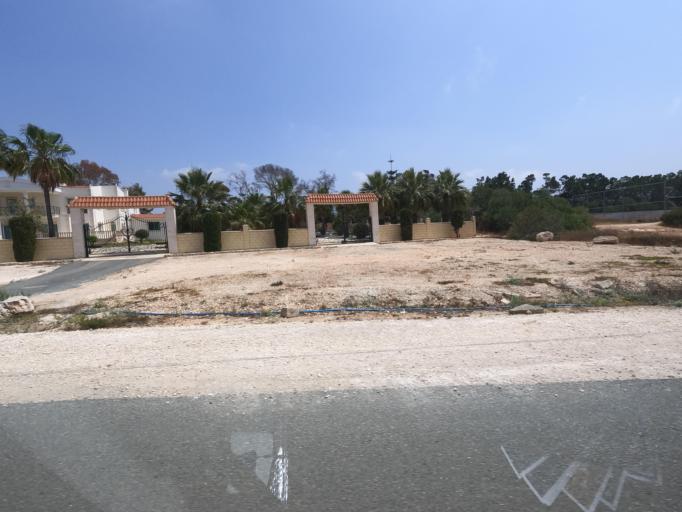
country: CY
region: Ammochostos
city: Ayia Napa
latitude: 34.9921
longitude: 34.0117
